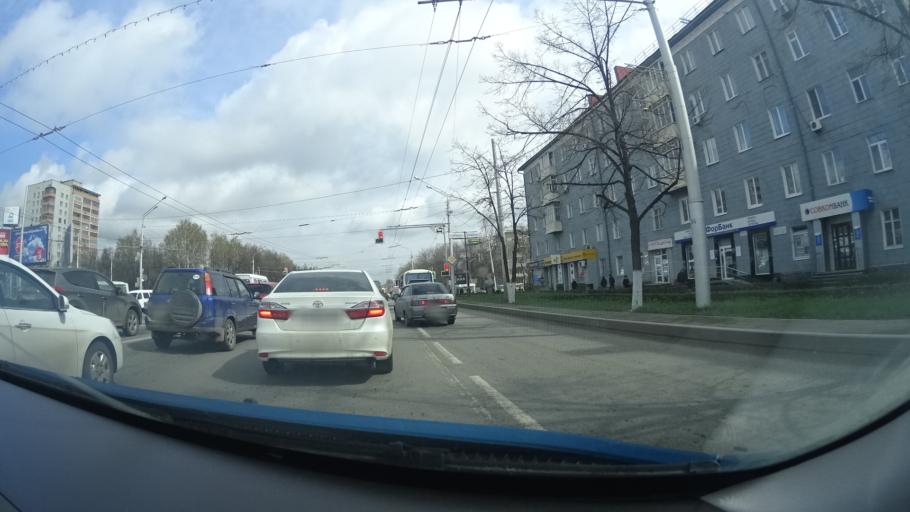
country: RU
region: Bashkortostan
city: Ufa
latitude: 54.7458
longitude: 55.9893
